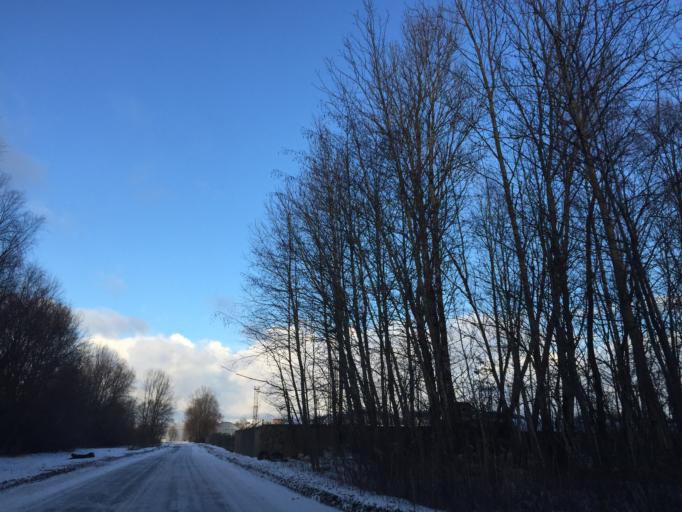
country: LV
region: Riga
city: Riga
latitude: 56.9851
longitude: 24.1101
